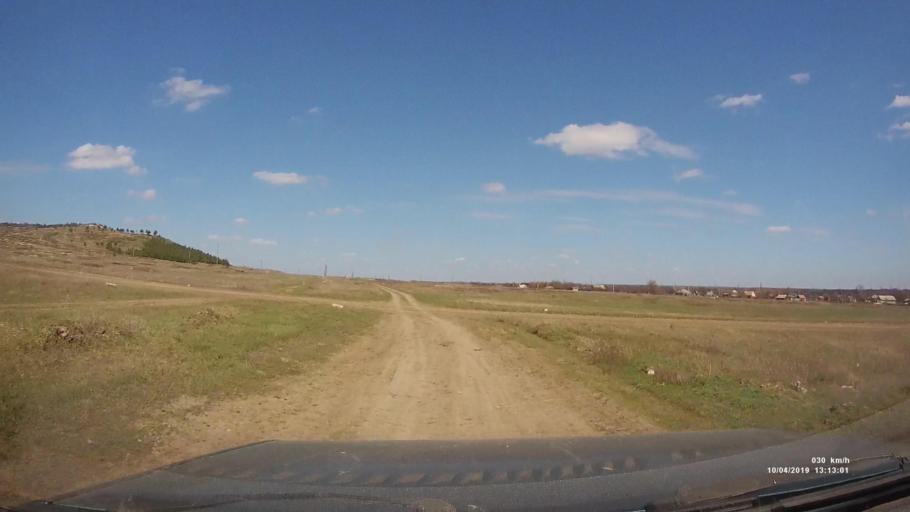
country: RU
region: Rostov
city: Masalovka
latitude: 48.4153
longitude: 40.2580
